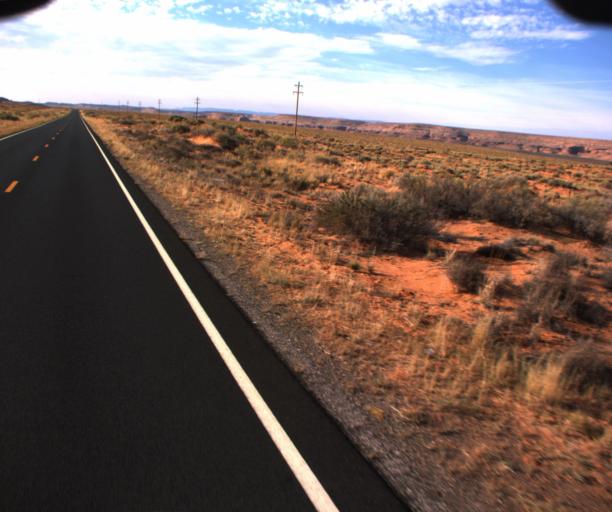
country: US
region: Arizona
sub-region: Apache County
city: Many Farms
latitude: 36.8034
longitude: -109.6483
